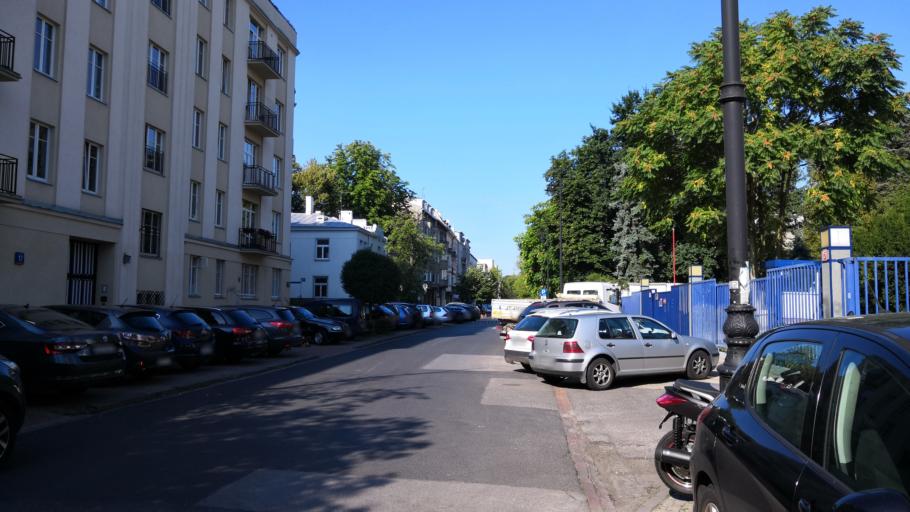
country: PL
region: Masovian Voivodeship
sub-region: Warszawa
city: Mokotow
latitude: 52.2068
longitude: 21.0185
